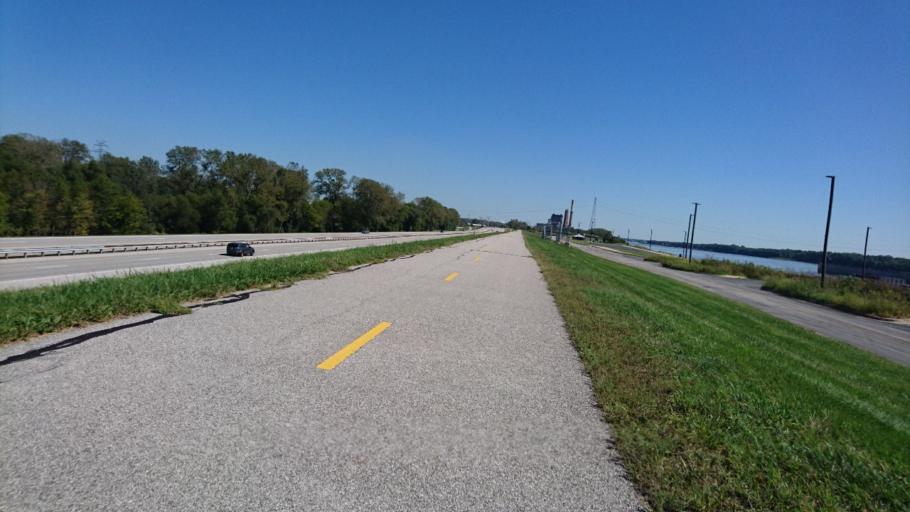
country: US
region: Illinois
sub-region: Madison County
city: Alton
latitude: 38.8713
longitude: -90.1500
